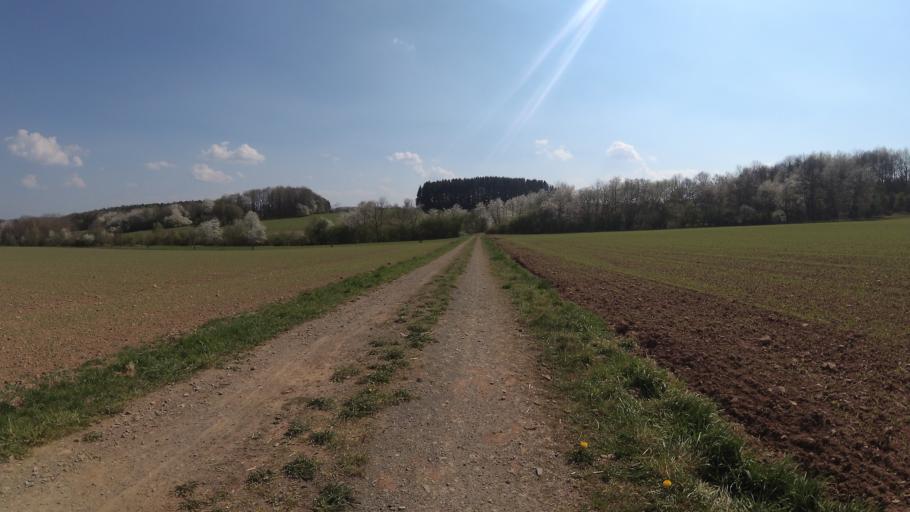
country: DE
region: Rheinland-Pfalz
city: Reichweiler
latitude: 49.5367
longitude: 7.2689
